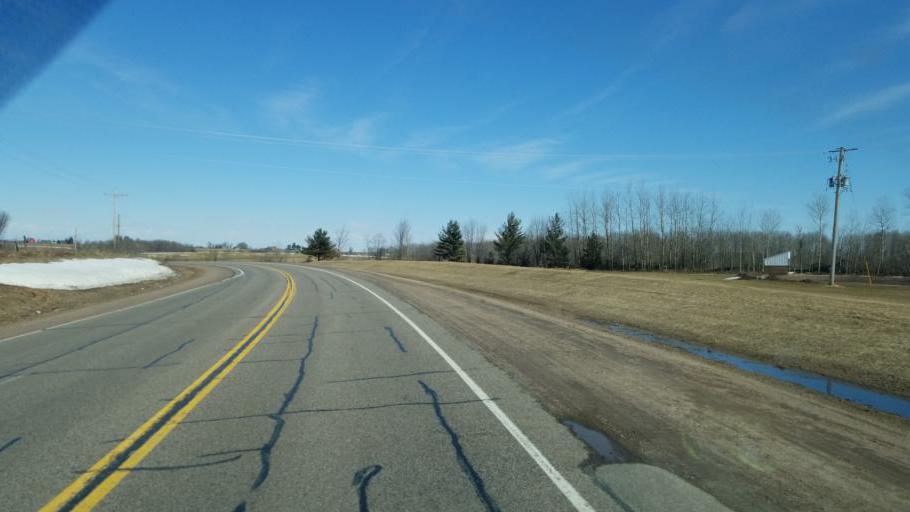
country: US
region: Wisconsin
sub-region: Marathon County
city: Spencer
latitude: 44.5841
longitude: -90.3779
